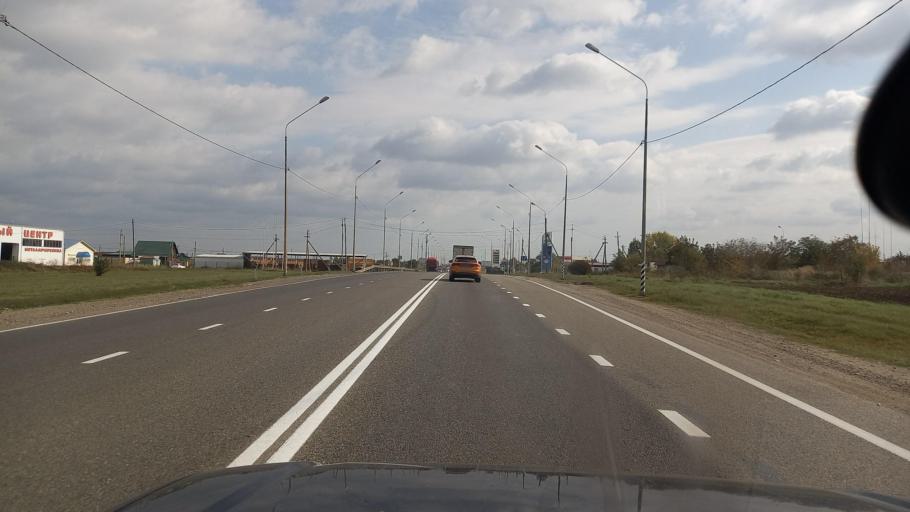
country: RU
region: Krasnodarskiy
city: Il'skiy
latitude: 44.8462
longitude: 38.5470
